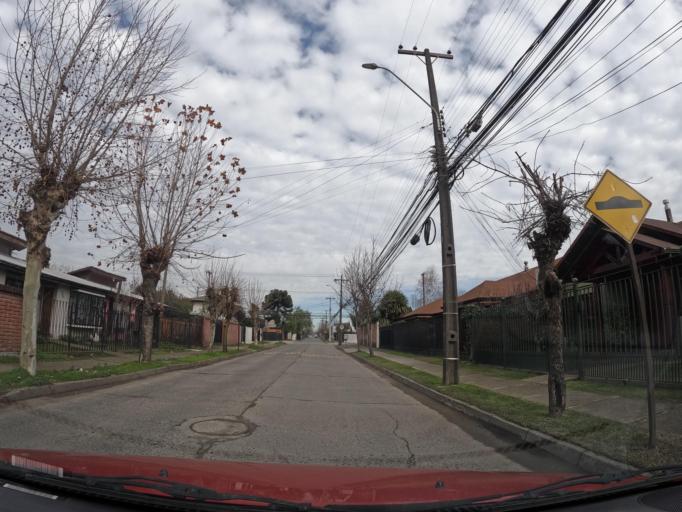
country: CL
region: Maule
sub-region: Provincia de Linares
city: Linares
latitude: -35.8392
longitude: -71.6031
